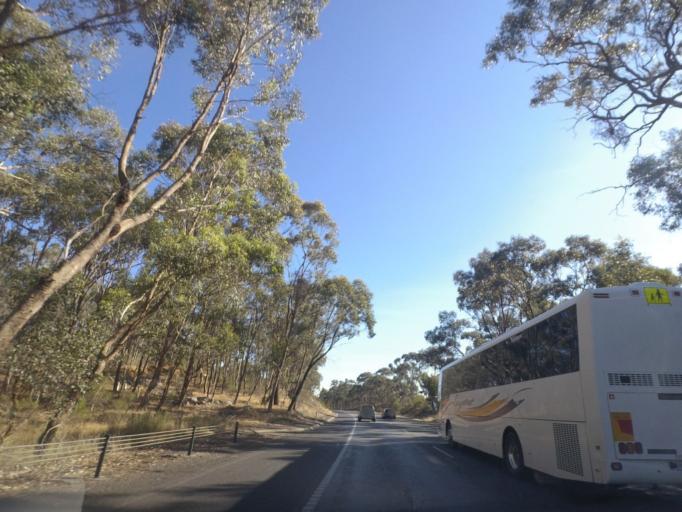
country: AU
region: Victoria
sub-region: Murrindindi
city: Kinglake West
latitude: -37.1780
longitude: 145.0706
